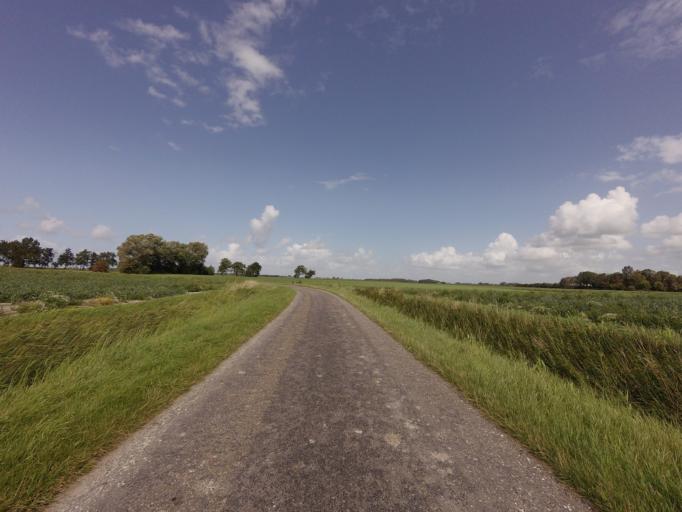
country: NL
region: Friesland
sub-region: Gemeente Harlingen
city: Harlingen
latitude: 53.1214
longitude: 5.4419
